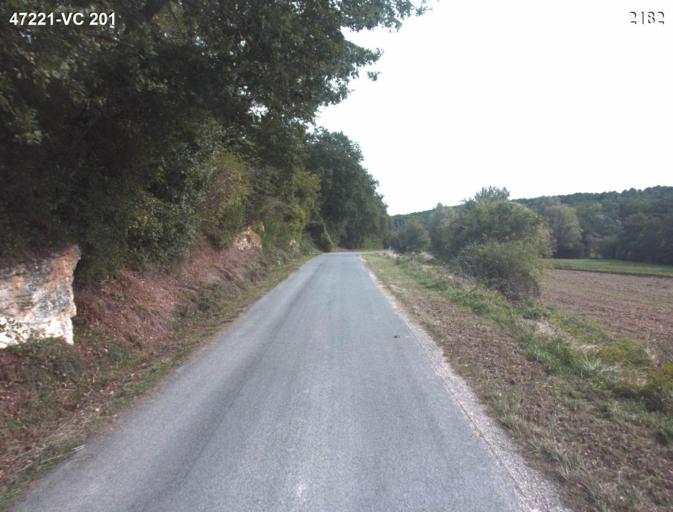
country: FR
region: Aquitaine
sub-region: Departement du Lot-et-Garonne
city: Mezin
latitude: 44.1099
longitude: 0.2453
